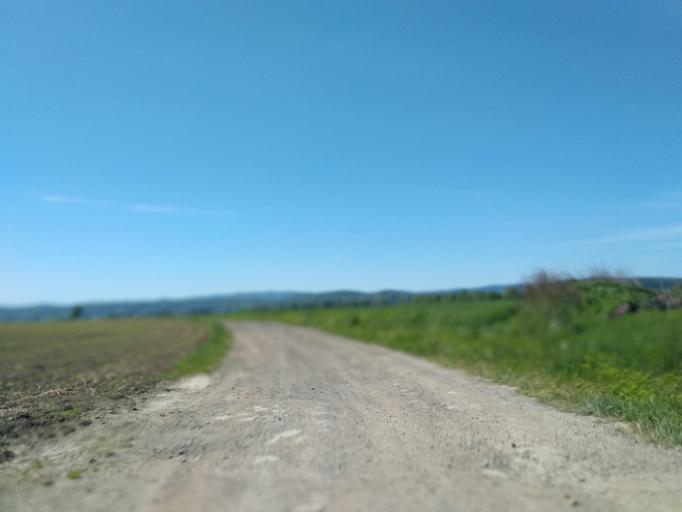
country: PL
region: Subcarpathian Voivodeship
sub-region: Powiat sanocki
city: Besko
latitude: 49.6191
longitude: 21.9715
